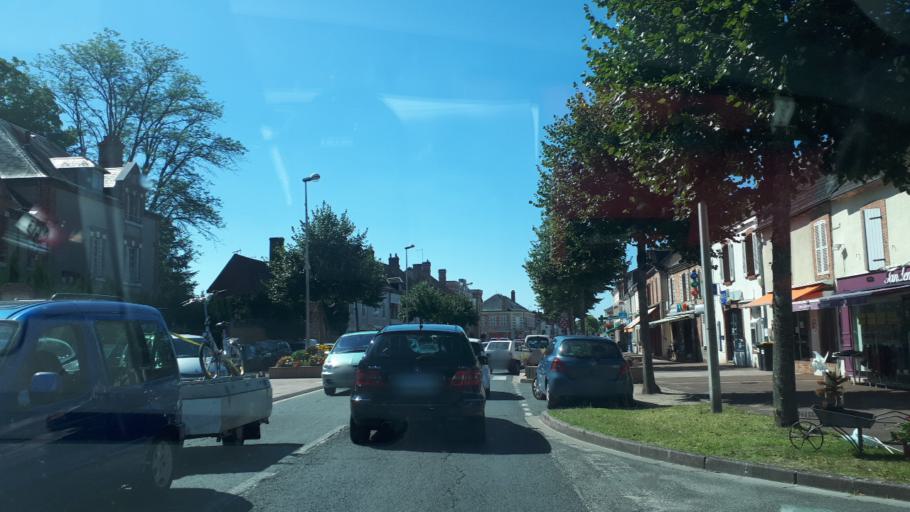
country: FR
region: Centre
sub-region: Departement du Loir-et-Cher
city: Lamotte-Beuvron
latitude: 47.6027
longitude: 2.0255
